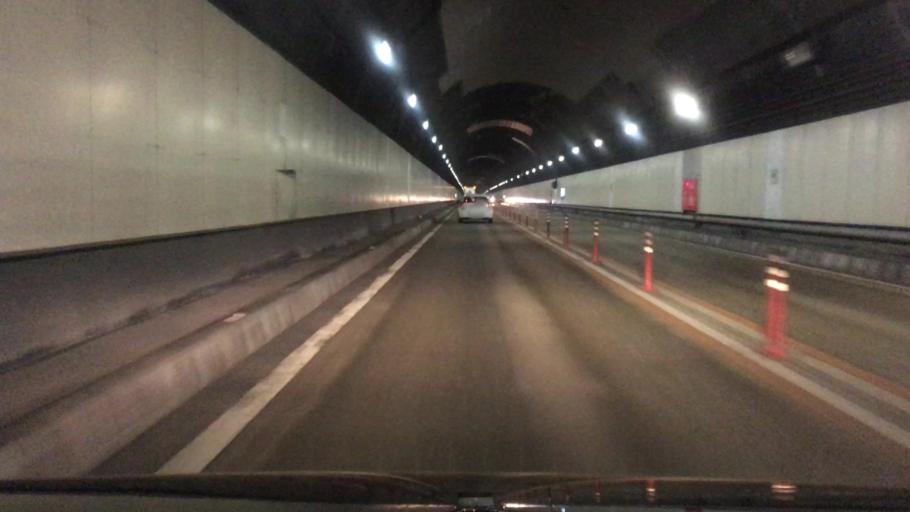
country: JP
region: Kyoto
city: Fukuchiyama
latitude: 35.2986
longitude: 134.9438
